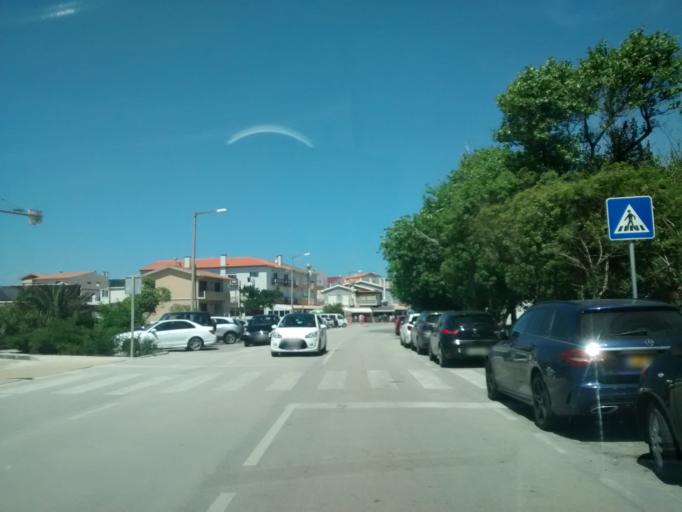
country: PT
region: Coimbra
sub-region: Mira
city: Mira
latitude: 40.4507
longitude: -8.8016
